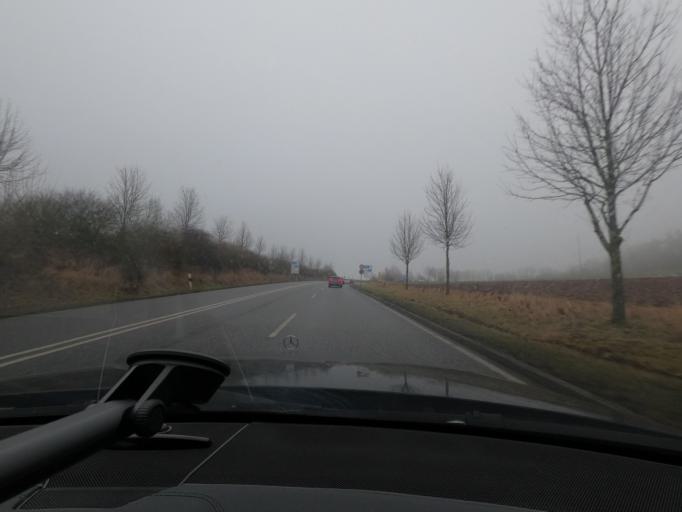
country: DE
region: Hesse
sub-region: Regierungsbezirk Kassel
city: Martinhagen
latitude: 51.3179
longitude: 9.2791
